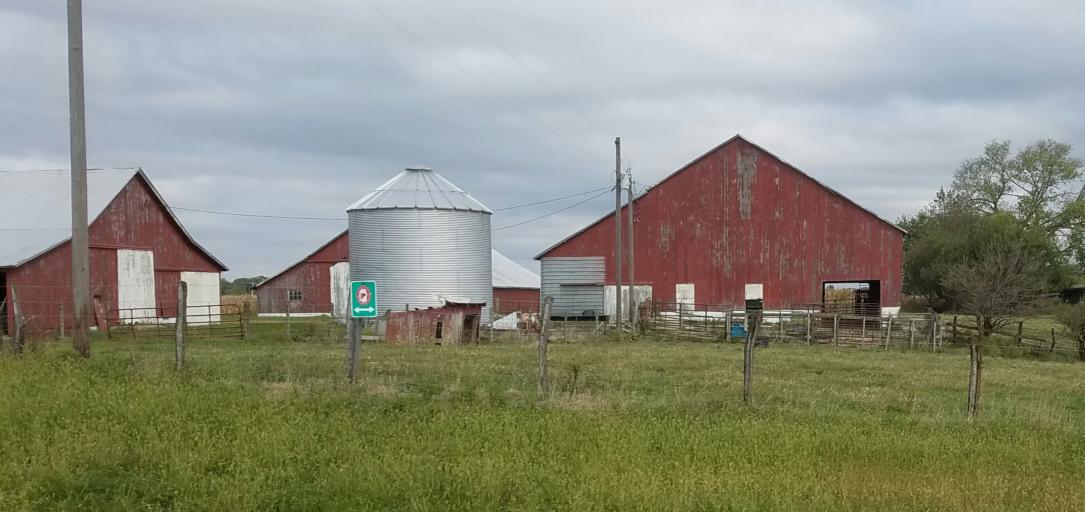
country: US
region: Illinois
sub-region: Fulton County
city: Lewistown
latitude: 40.3046
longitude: -90.1901
